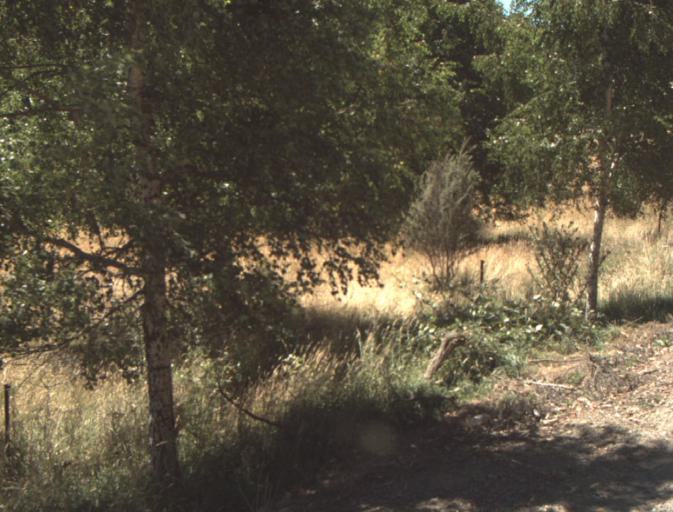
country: AU
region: Tasmania
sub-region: Dorset
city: Scottsdale
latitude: -41.2948
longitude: 147.4004
